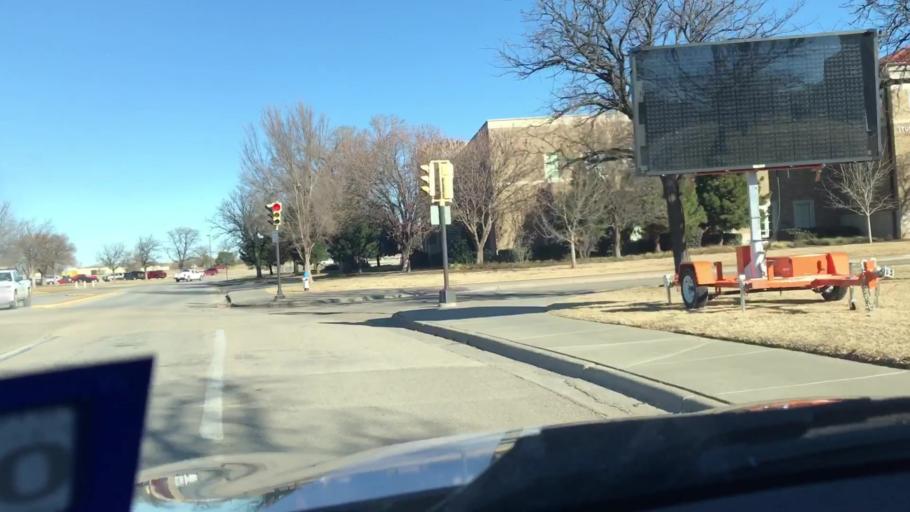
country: US
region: Texas
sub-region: Lubbock County
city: Lubbock
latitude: 33.5854
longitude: -101.8821
